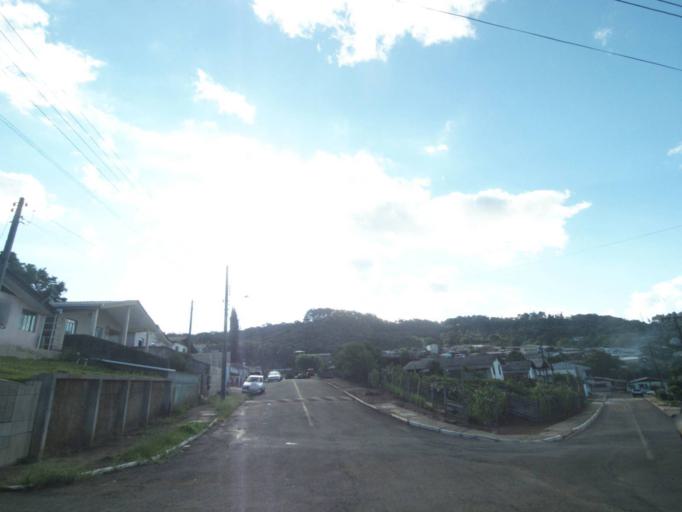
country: BR
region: Parana
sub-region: Uniao Da Vitoria
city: Uniao da Vitoria
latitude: -26.1677
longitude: -51.5346
